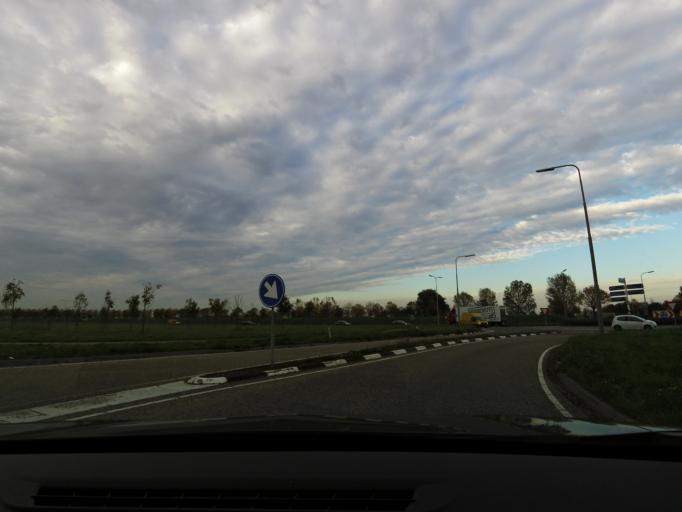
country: NL
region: South Holland
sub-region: Gemeente Goeree-Overflakkee
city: Dirksland
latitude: 51.7762
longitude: 4.0737
